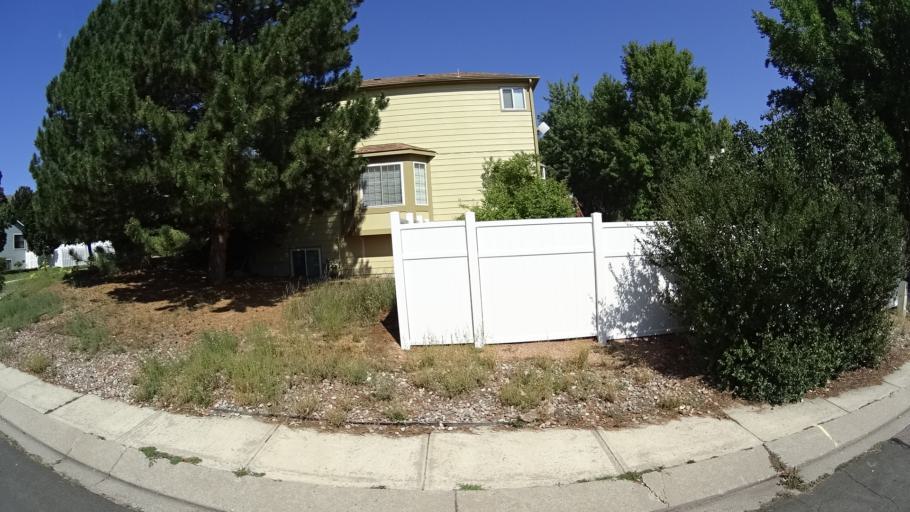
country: US
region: Colorado
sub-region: El Paso County
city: Air Force Academy
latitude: 38.9216
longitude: -104.8648
